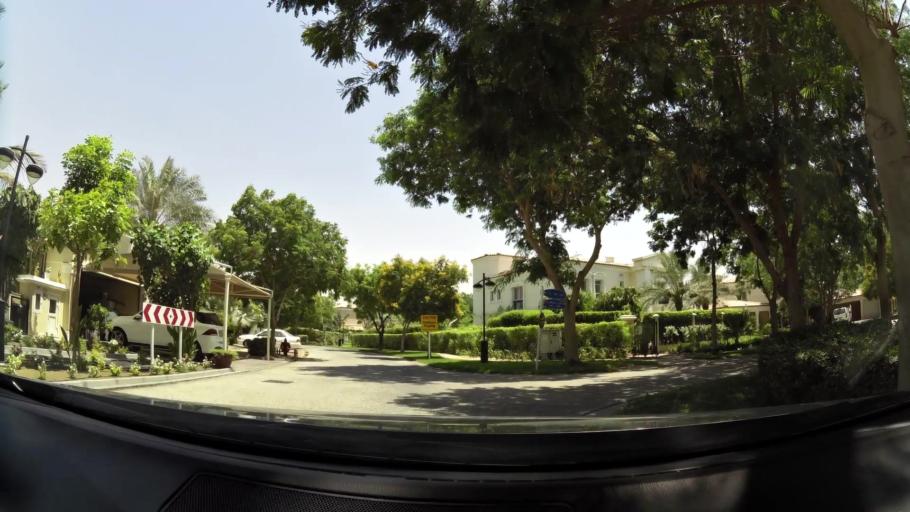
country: AE
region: Dubai
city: Dubai
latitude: 24.9959
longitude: 55.1650
